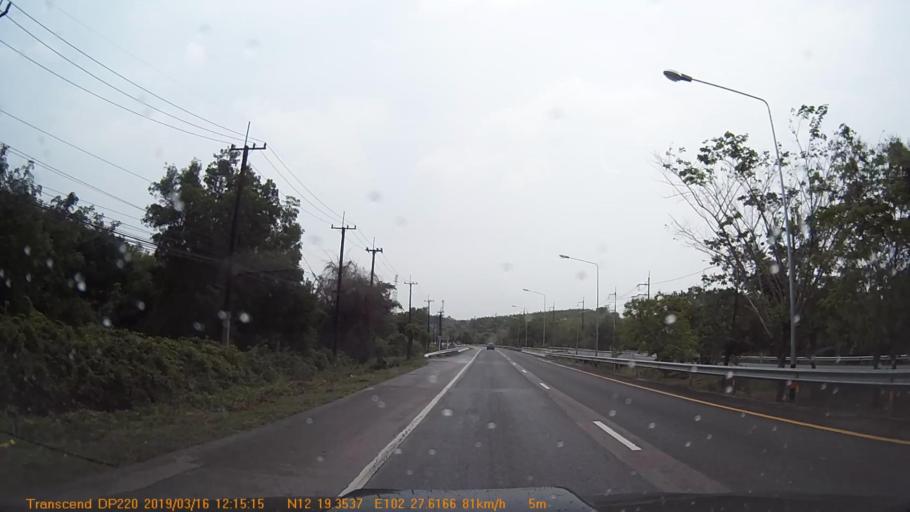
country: TH
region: Trat
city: Khao Saming
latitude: 12.3224
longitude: 102.4604
